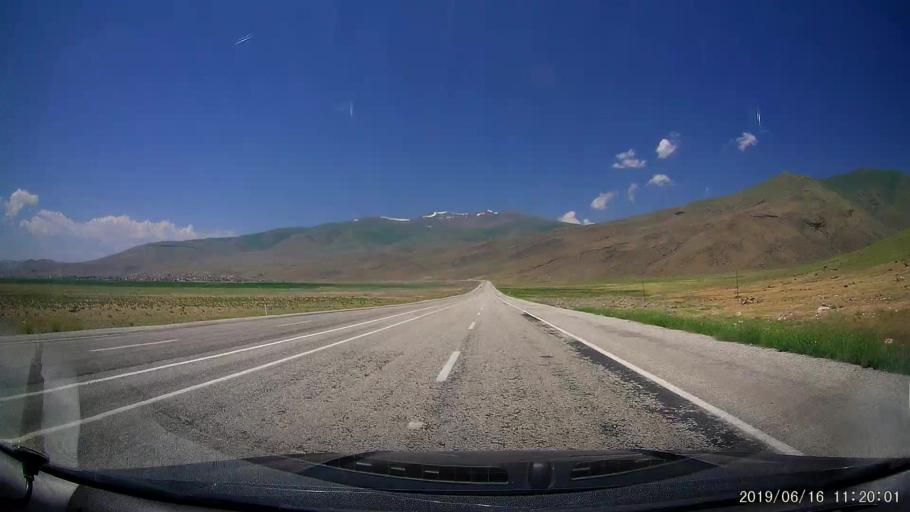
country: TR
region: Agri
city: Dogubayazit
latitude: 39.6965
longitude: 44.1012
